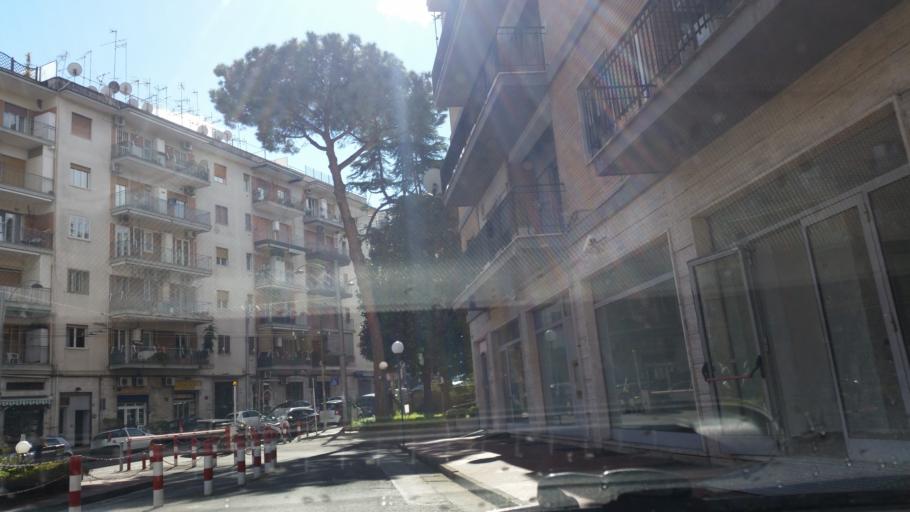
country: IT
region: Campania
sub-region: Provincia di Napoli
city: Napoli
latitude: 40.8715
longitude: 14.2396
